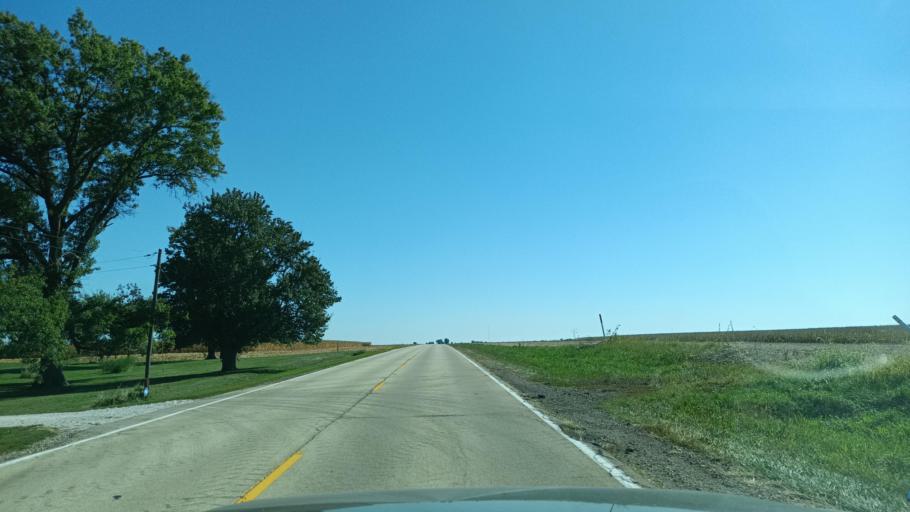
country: US
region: Illinois
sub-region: Peoria County
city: Elmwood
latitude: 40.9021
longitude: -89.9516
